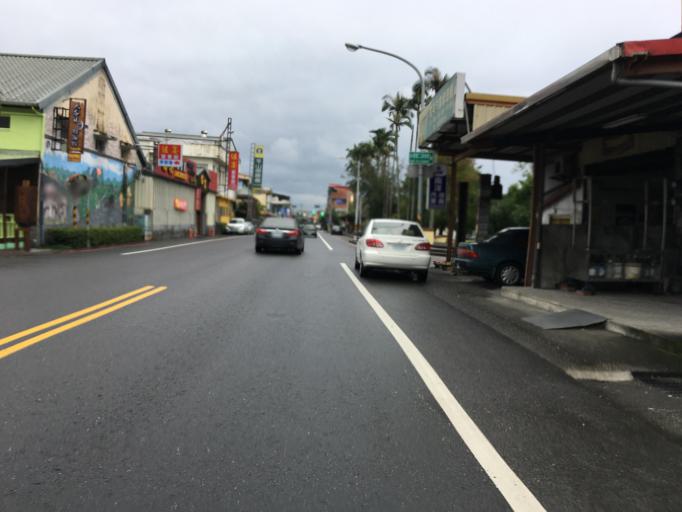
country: TW
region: Taiwan
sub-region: Yilan
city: Yilan
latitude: 24.6551
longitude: 121.7620
